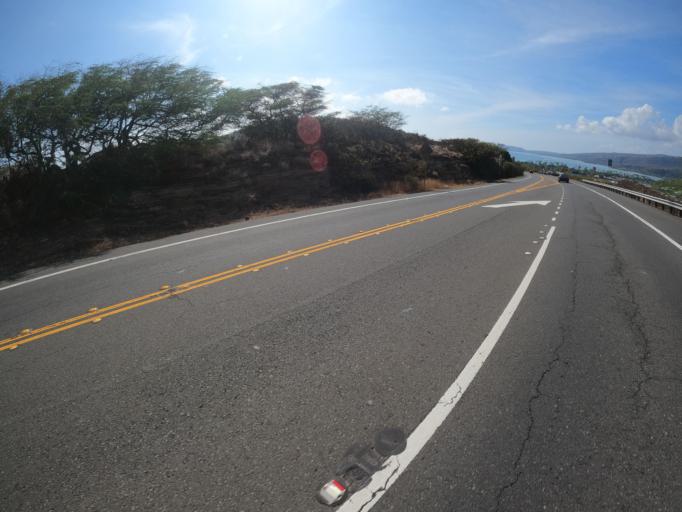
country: US
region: Hawaii
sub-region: Honolulu County
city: Waimanalo Beach
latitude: 21.2750
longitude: -157.6945
